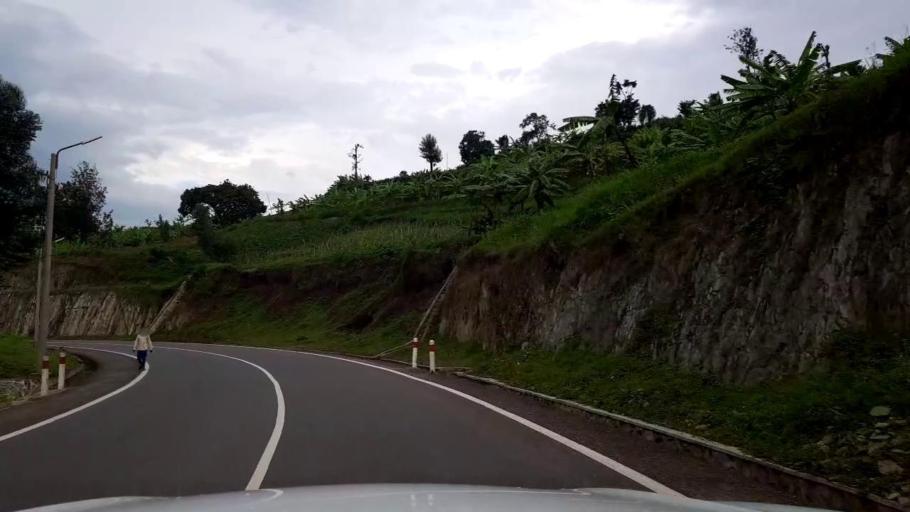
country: RW
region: Western Province
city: Kibuye
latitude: -2.0399
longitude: 29.4046
